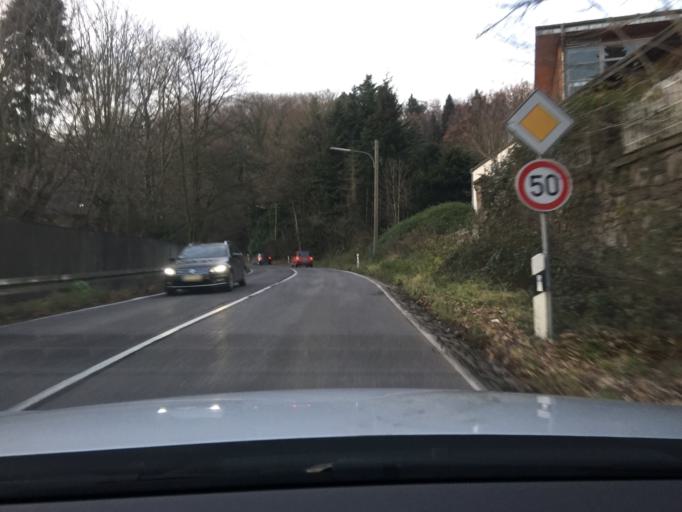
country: DE
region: North Rhine-Westphalia
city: Hattingen
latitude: 51.3757
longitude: 7.1330
